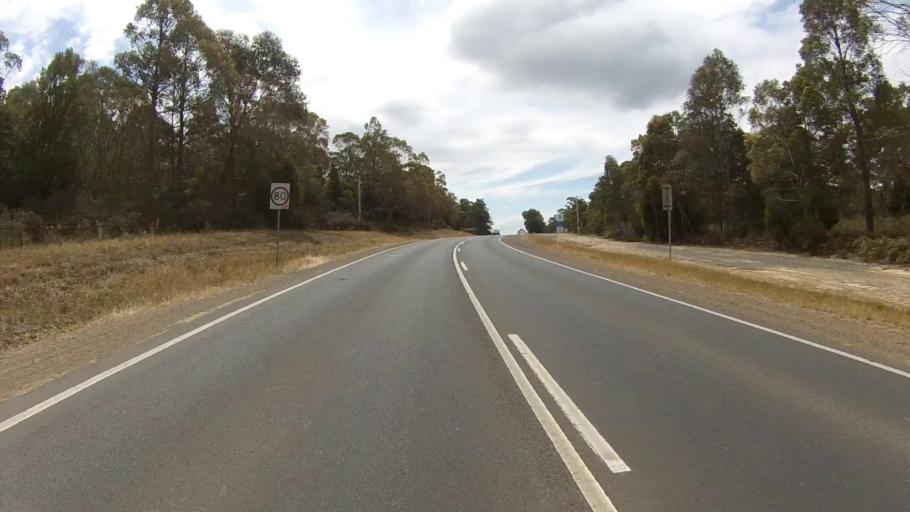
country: AU
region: Tasmania
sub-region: Kingborough
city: Margate
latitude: -43.0495
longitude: 147.2625
